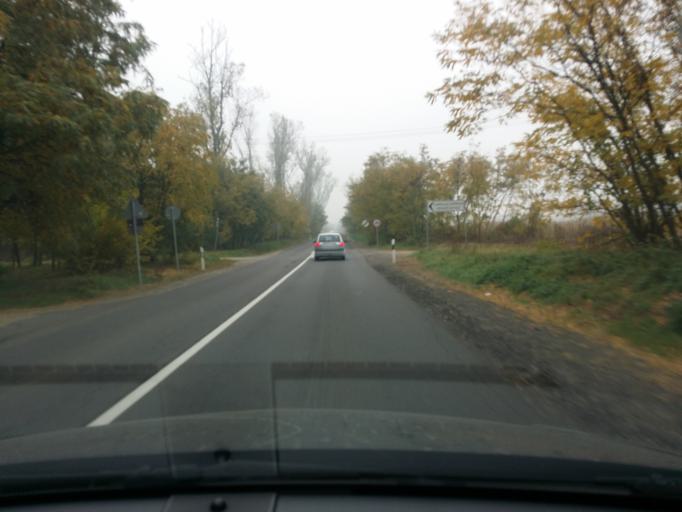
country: HU
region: Szabolcs-Szatmar-Bereg
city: Nyirpazony
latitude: 48.0046
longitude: 21.8219
